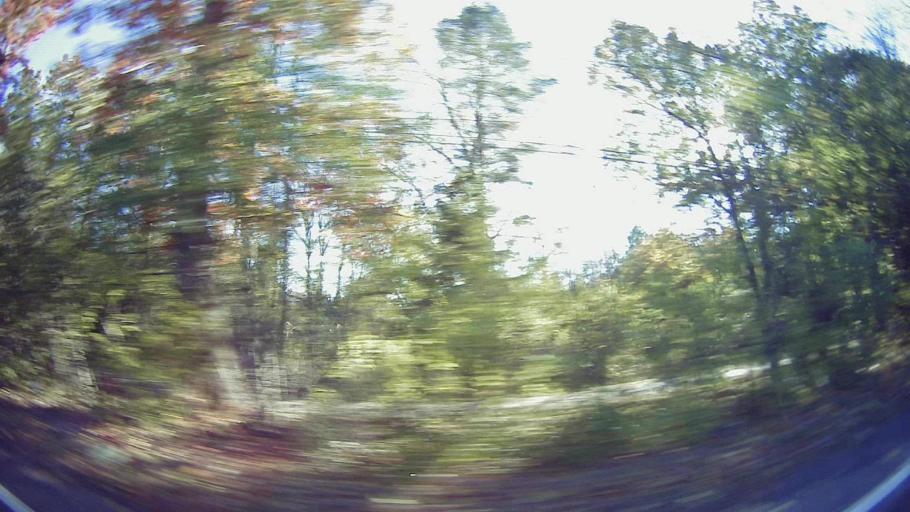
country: US
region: Michigan
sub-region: Oakland County
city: Franklin
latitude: 42.5443
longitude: -83.3066
